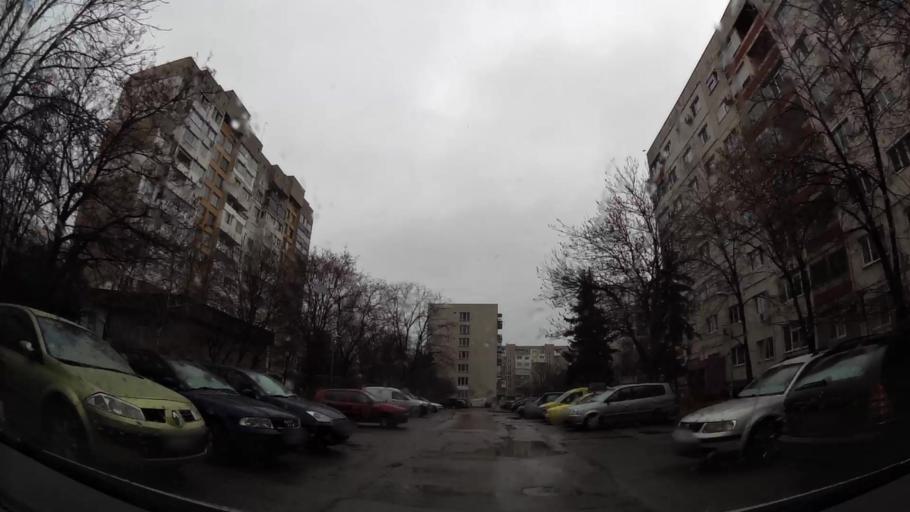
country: BG
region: Sofia-Capital
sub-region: Stolichna Obshtina
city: Sofia
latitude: 42.6588
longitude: 23.4007
